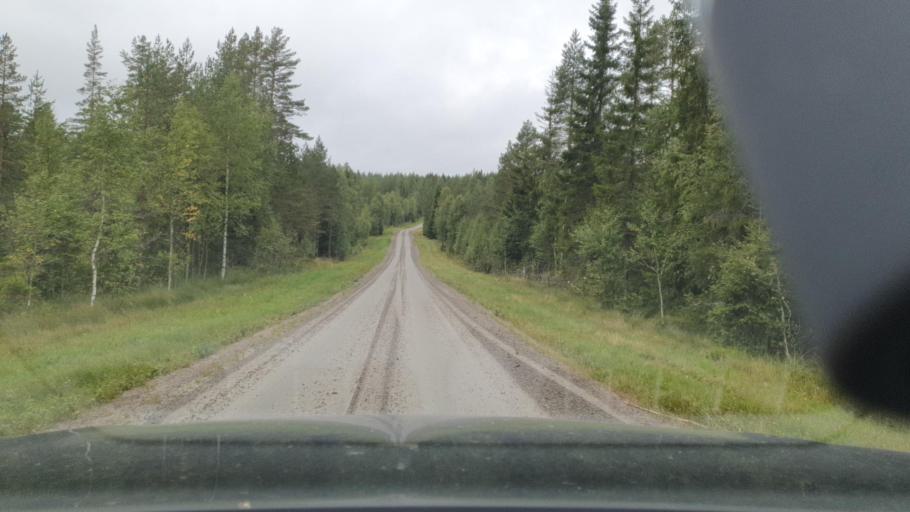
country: SE
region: Vaermland
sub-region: Torsby Kommun
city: Torsby
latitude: 60.4466
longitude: 12.9585
